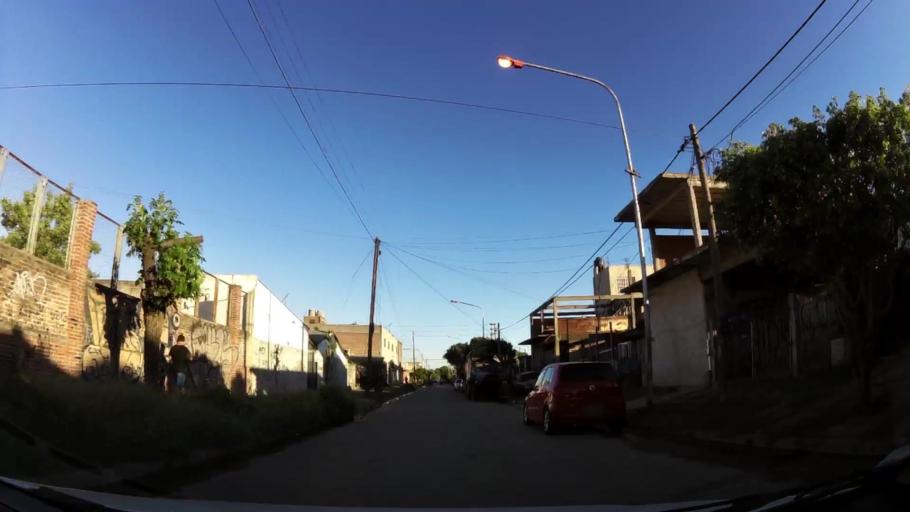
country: AR
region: Buenos Aires
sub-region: Partido de Moron
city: Moron
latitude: -34.7170
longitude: -58.6135
